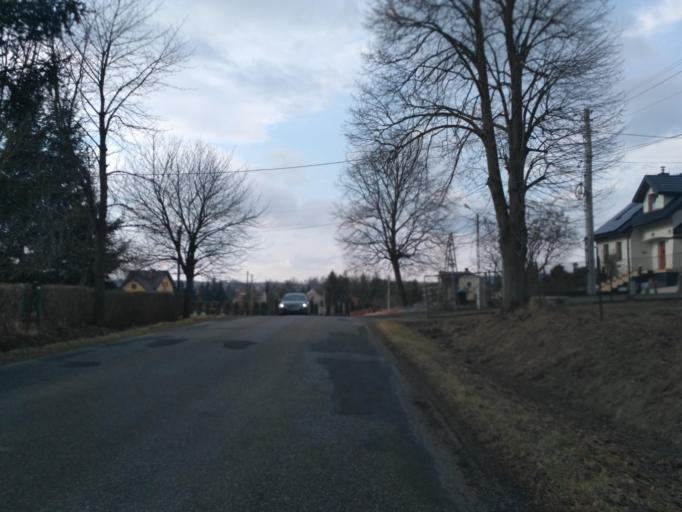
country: PL
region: Subcarpathian Voivodeship
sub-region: Powiat sanocki
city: Strachocina
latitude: 49.6089
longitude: 22.0958
